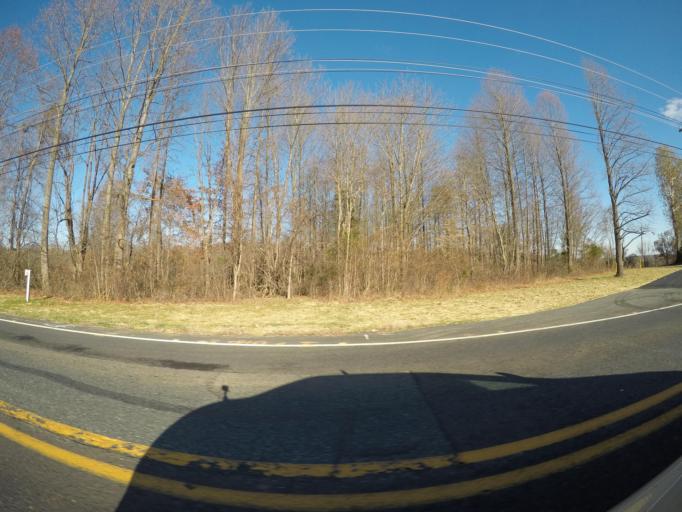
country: US
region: Maryland
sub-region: Harford County
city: South Bel Air
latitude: 39.6242
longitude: -76.2607
